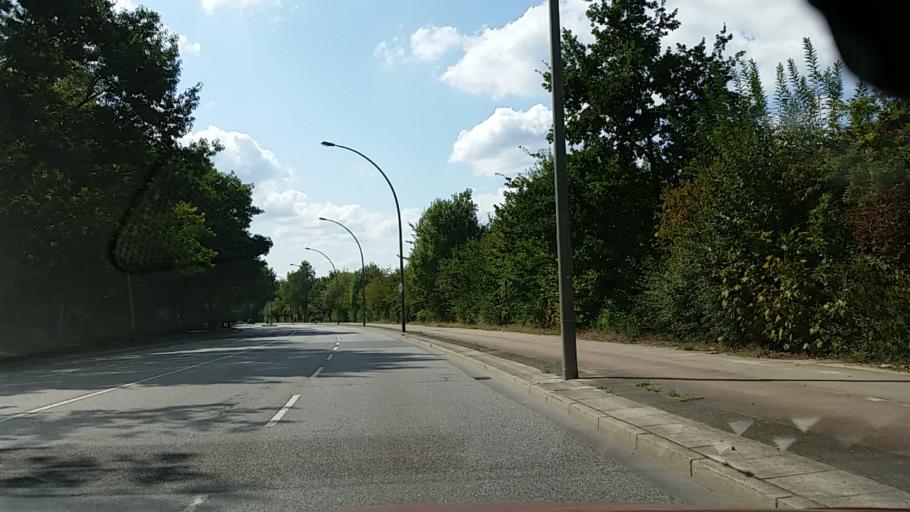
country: DE
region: Hamburg
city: Farmsen-Berne
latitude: 53.6229
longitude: 10.1296
